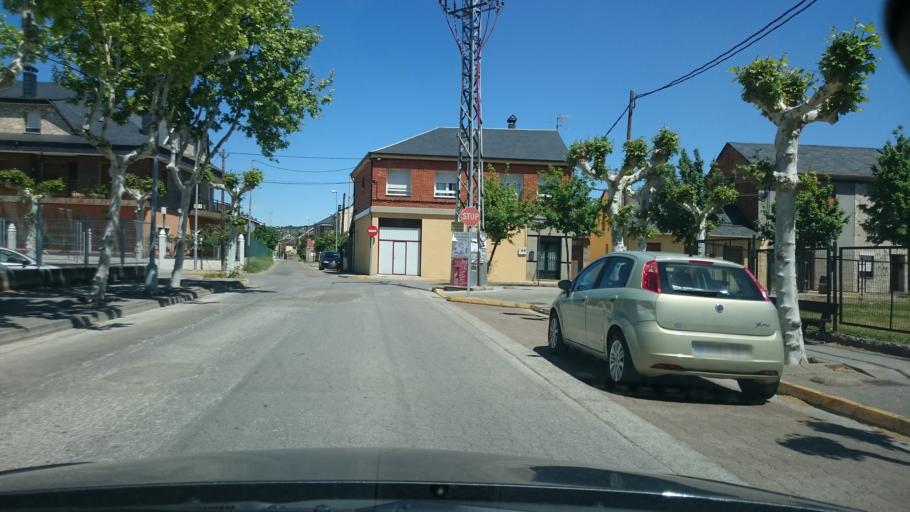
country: ES
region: Castille and Leon
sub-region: Provincia de Leon
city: Camponaraya
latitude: 42.5736
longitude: -6.6424
